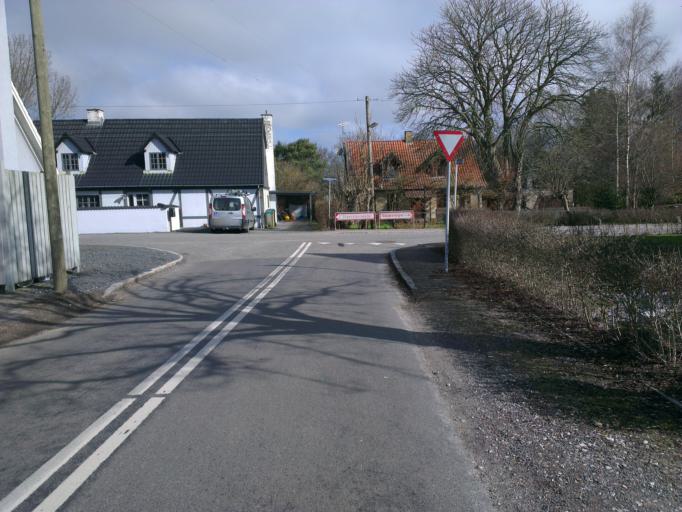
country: DK
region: Capital Region
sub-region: Hillerod Kommune
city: Skaevinge
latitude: 55.8826
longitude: 12.1274
